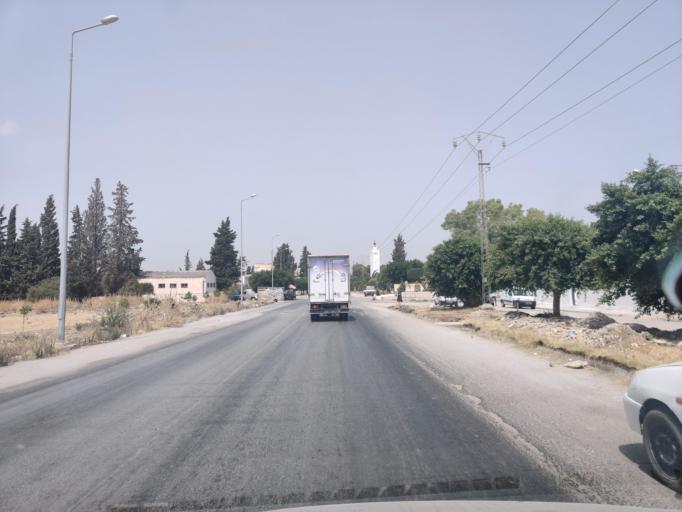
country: TN
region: Tunis
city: La Sebala du Mornag
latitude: 36.6608
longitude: 10.3263
